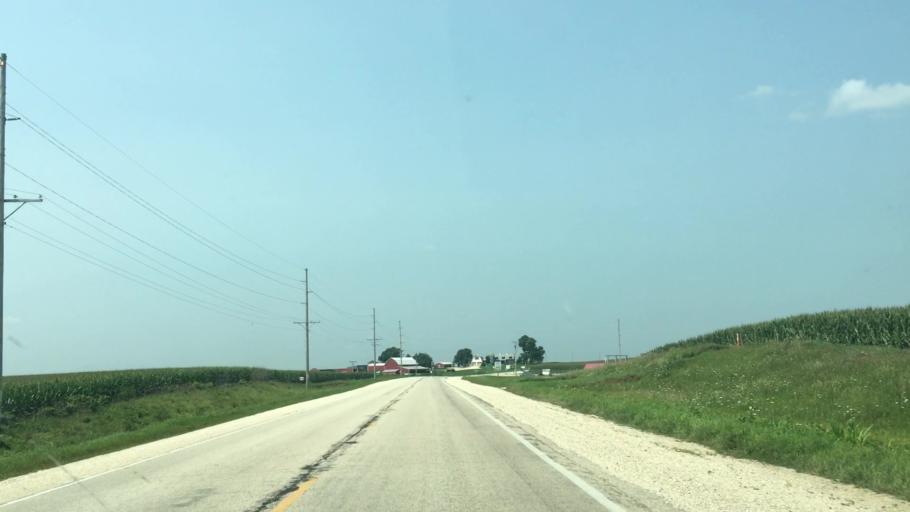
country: US
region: Iowa
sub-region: Fayette County
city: West Union
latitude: 42.9764
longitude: -91.8215
